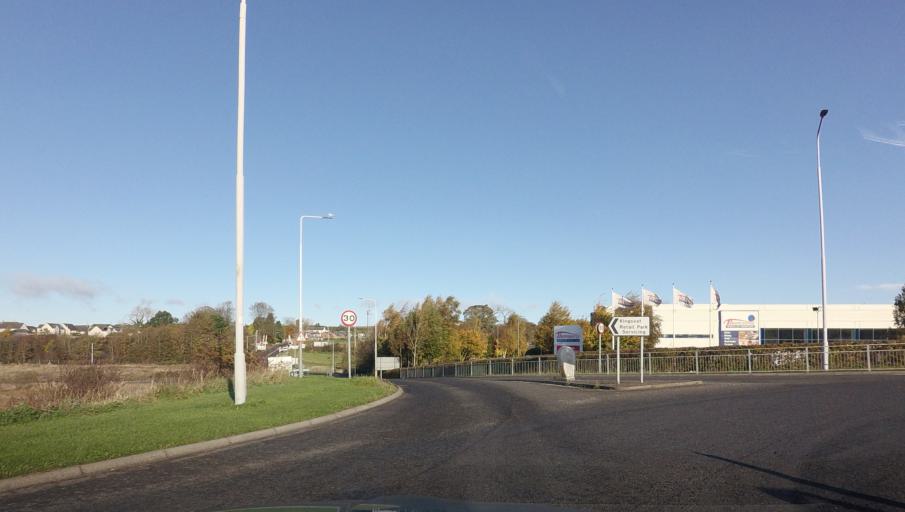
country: GB
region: Scotland
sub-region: Fife
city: Crossgates
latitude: 56.0820
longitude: -3.4037
